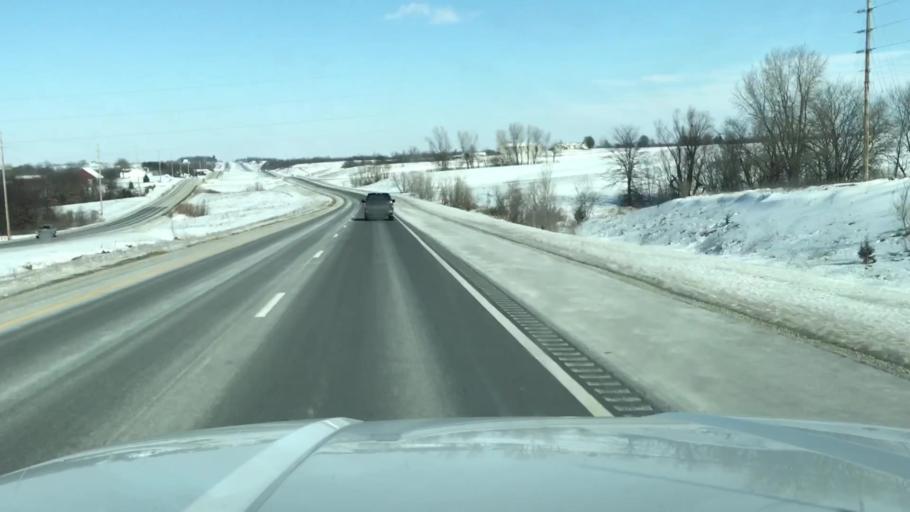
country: US
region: Missouri
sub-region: Nodaway County
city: Maryville
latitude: 40.1817
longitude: -94.8683
